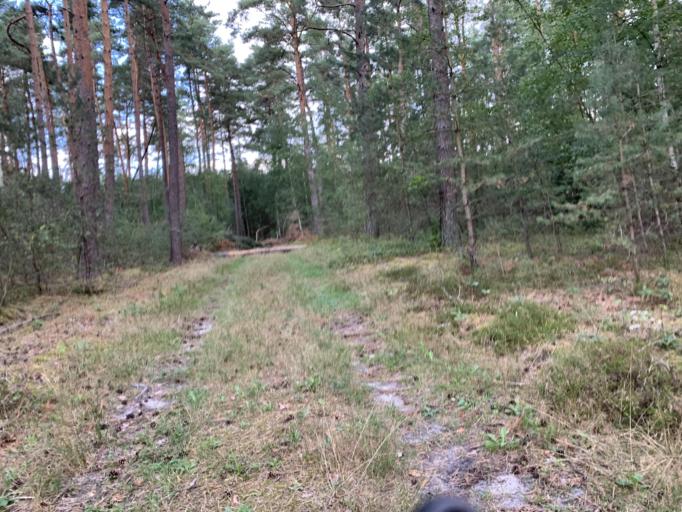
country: DE
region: Lower Saxony
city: Reinstorf
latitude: 53.2155
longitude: 10.6106
